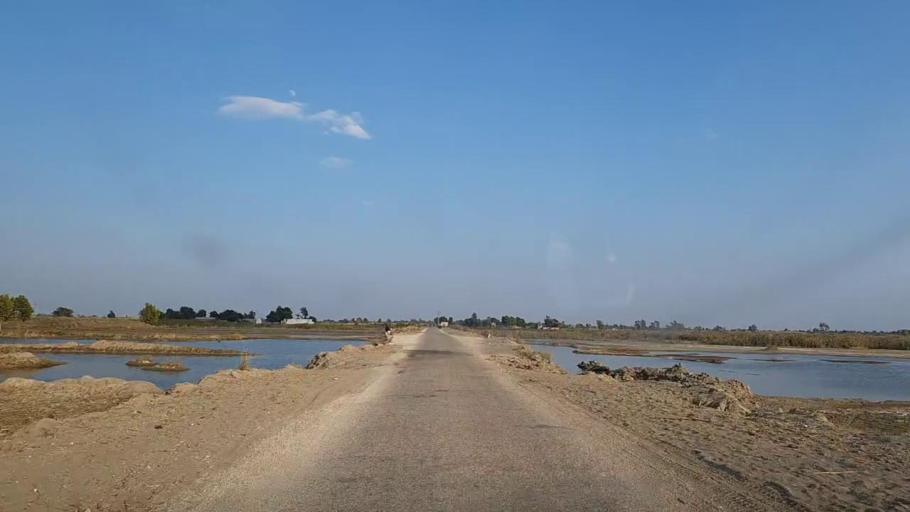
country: PK
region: Sindh
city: Sanghar
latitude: 26.2644
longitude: 68.9502
